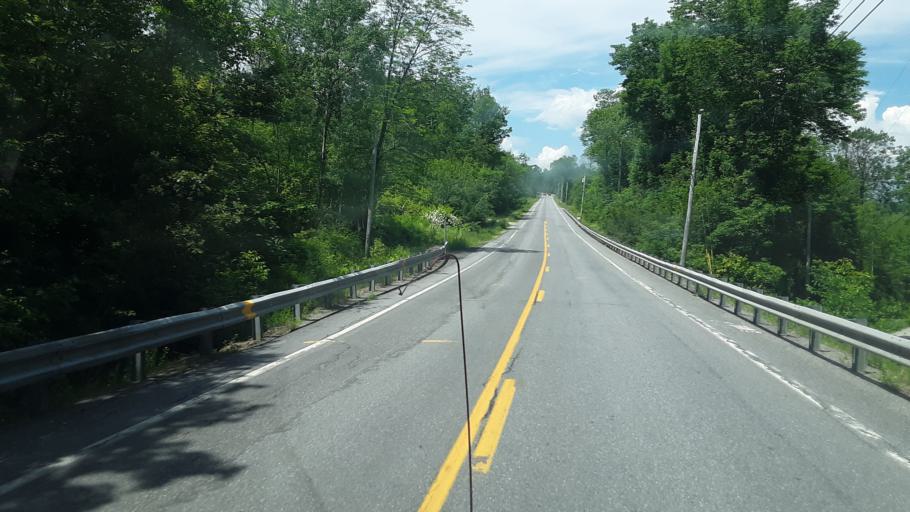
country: US
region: Maine
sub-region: Hancock County
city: Bucksport
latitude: 44.5693
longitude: -68.8112
